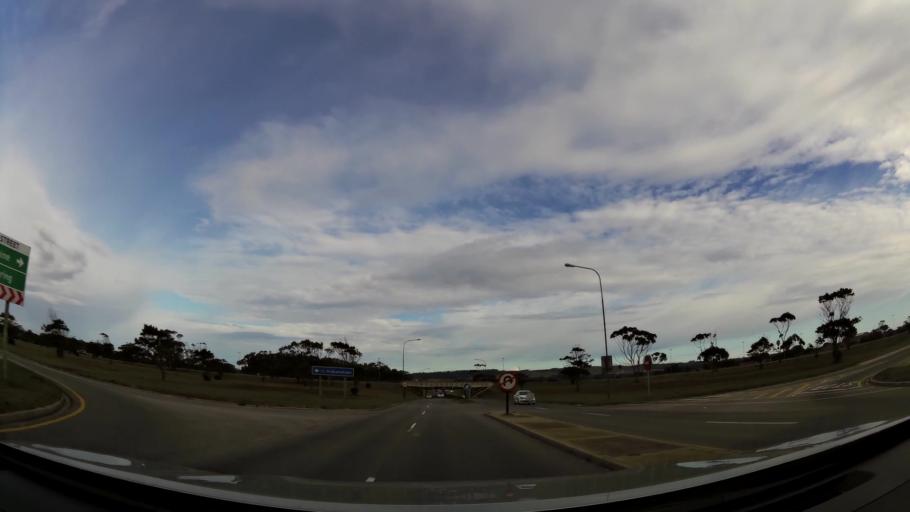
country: ZA
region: Eastern Cape
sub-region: Nelson Mandela Bay Metropolitan Municipality
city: Port Elizabeth
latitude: -33.9467
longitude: 25.5108
